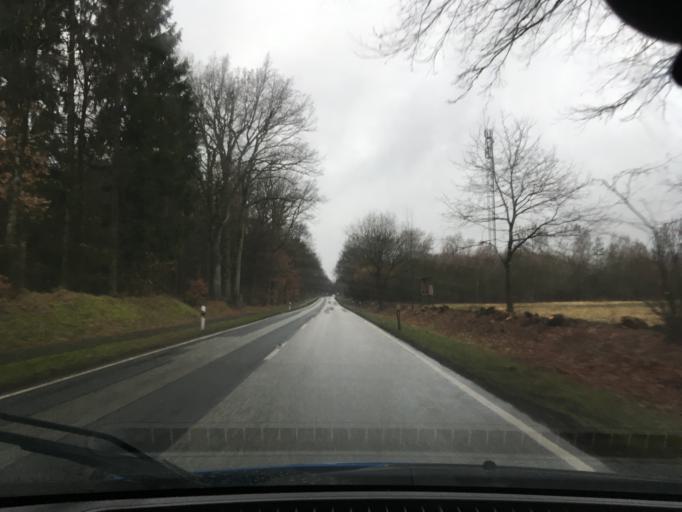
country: DE
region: Schleswig-Holstein
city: Schnakenbek
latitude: 53.3907
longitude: 10.4862
